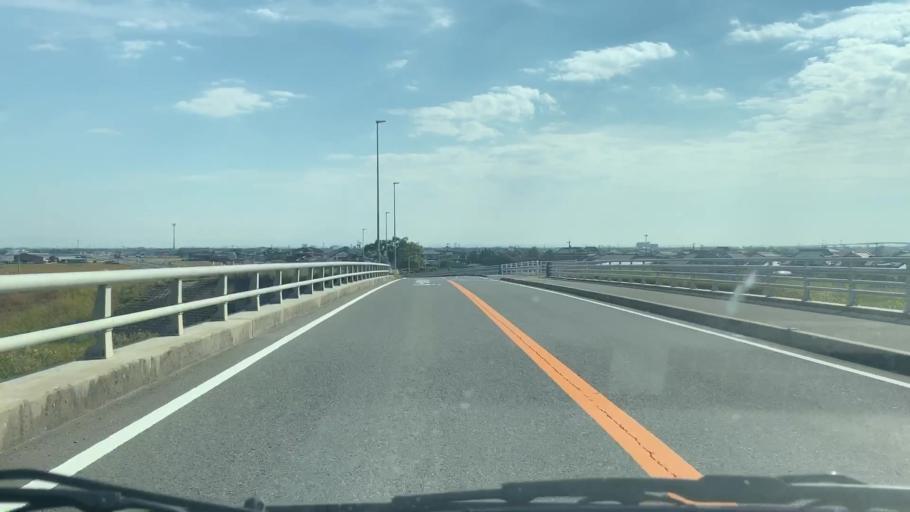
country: JP
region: Saga Prefecture
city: Saga-shi
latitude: 33.2220
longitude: 130.1939
